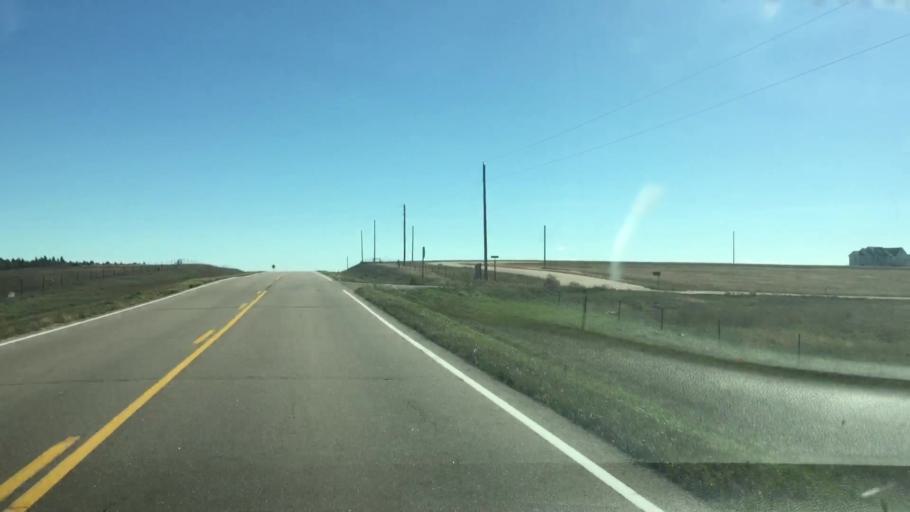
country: US
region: Colorado
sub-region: Lincoln County
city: Limon
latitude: 39.2735
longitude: -104.0239
